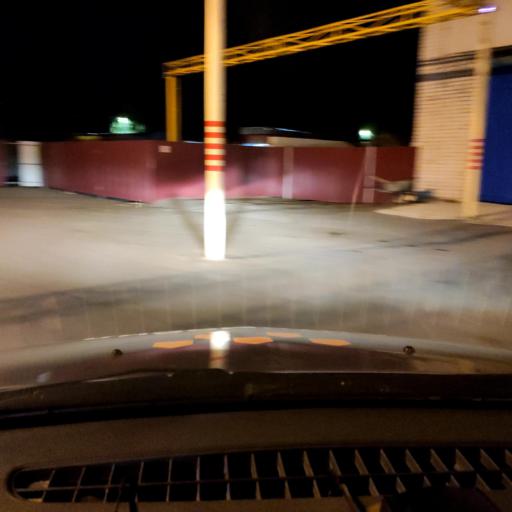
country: RU
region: Voronezj
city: Voronezh
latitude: 51.6775
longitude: 39.2658
